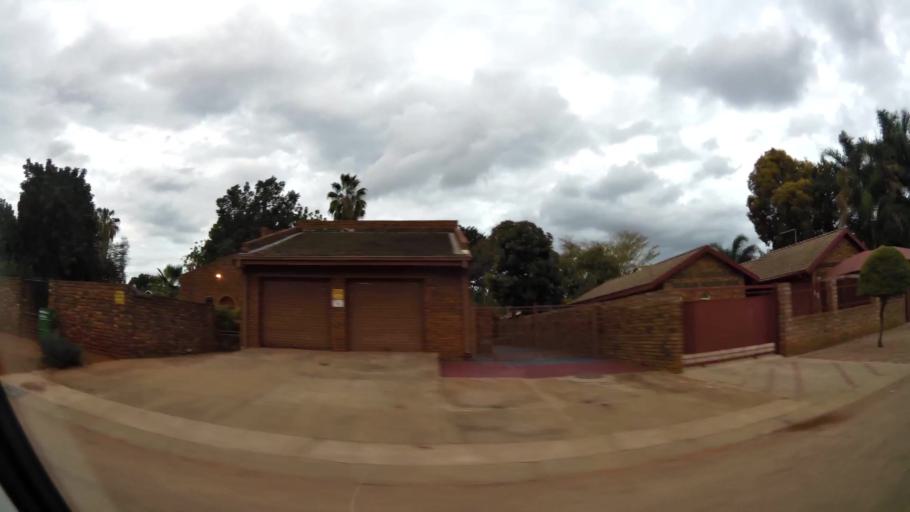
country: ZA
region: Limpopo
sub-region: Waterberg District Municipality
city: Mokopane
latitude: -24.1850
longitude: 28.9917
